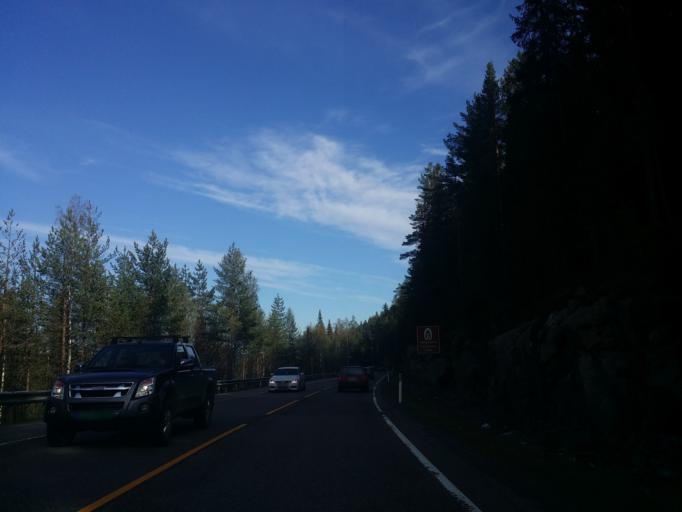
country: NO
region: Buskerud
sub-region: Kongsberg
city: Kongsberg
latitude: 59.6289
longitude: 9.5704
